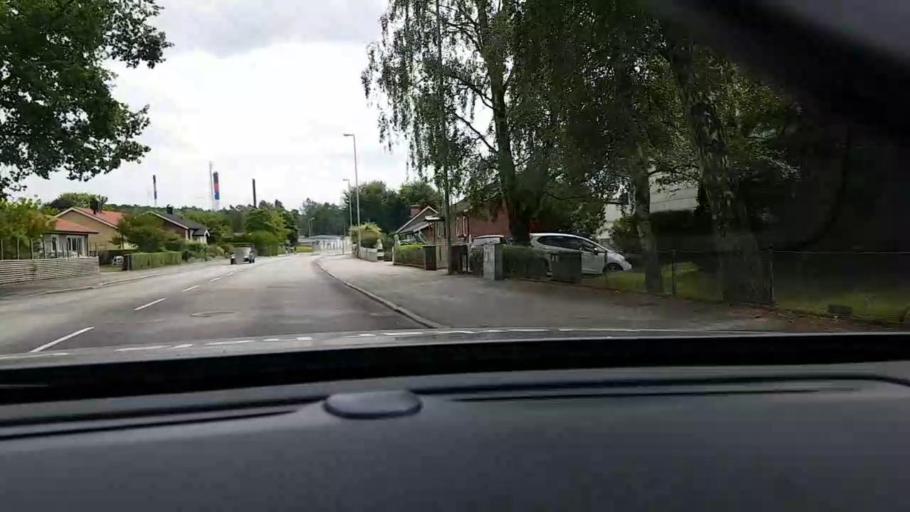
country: SE
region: Skane
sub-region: Hassleholms Kommun
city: Hassleholm
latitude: 56.1680
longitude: 13.7842
